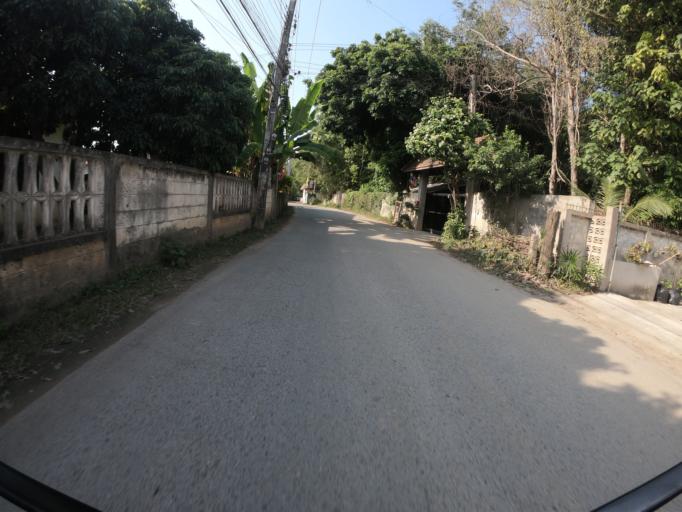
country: TH
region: Chiang Mai
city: Chiang Mai
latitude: 18.8497
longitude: 98.9829
